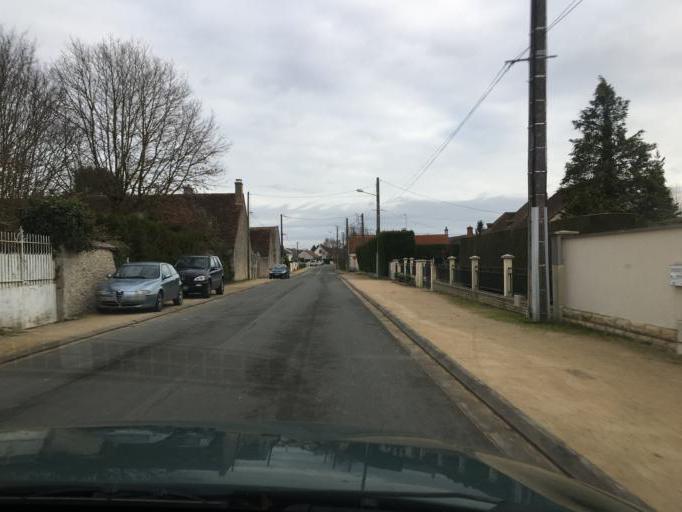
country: FR
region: Centre
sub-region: Departement du Loiret
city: Baule
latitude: 47.8452
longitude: 1.6543
